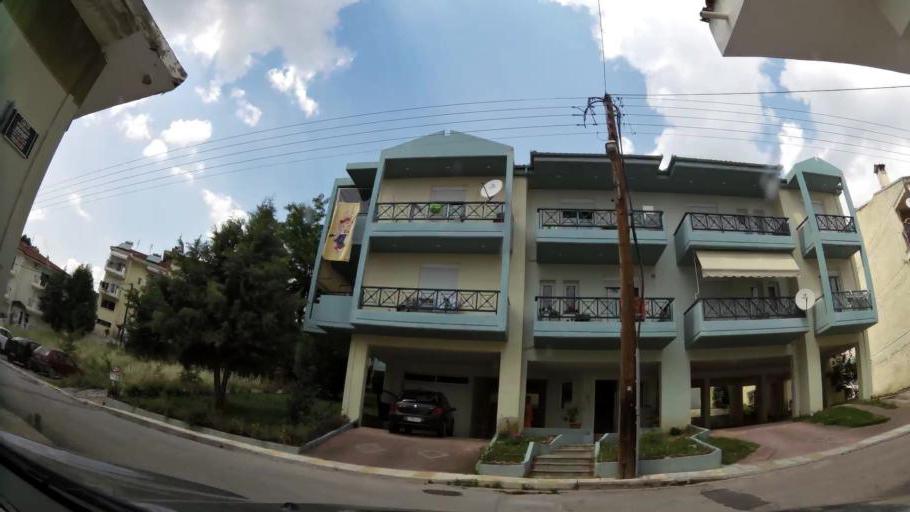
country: GR
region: West Macedonia
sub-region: Nomos Kozanis
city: Kozani
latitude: 40.3091
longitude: 21.7859
